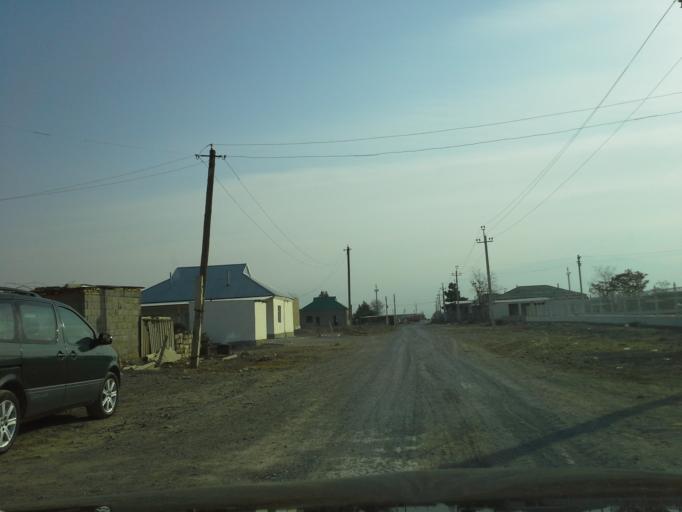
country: TM
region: Ahal
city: Abadan
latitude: 38.1768
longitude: 58.0456
